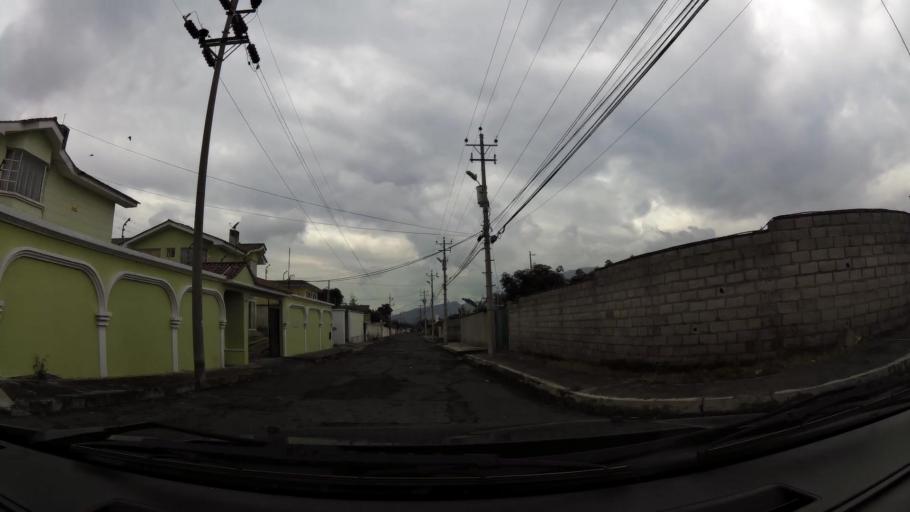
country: EC
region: Pichincha
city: Sangolqui
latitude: -0.3070
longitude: -78.4658
